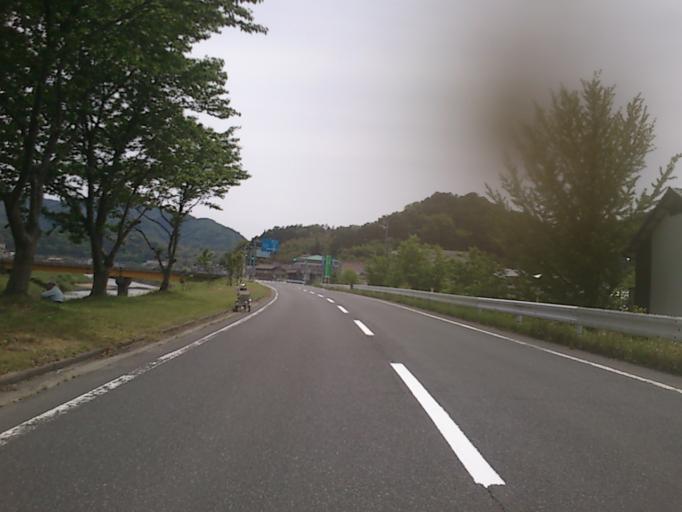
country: JP
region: Kyoto
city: Miyazu
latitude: 35.6607
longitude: 135.0868
